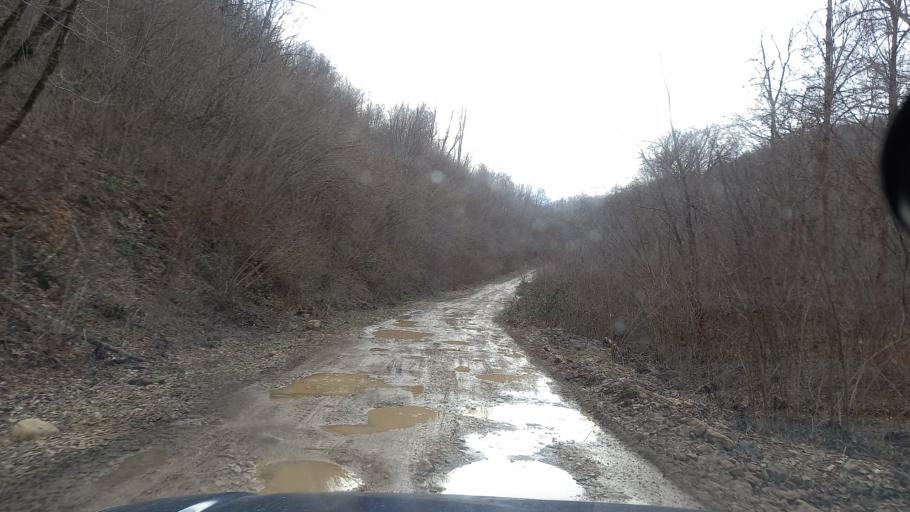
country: RU
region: Adygeya
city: Kamennomostskiy
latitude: 44.1740
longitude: 40.3002
